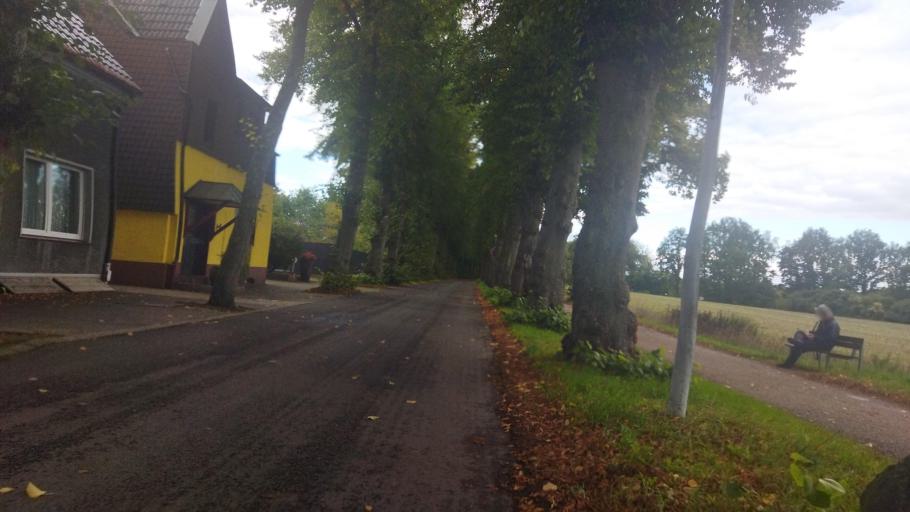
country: DE
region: North Rhine-Westphalia
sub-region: Regierungsbezirk Munster
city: Haltern
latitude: 51.7502
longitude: 7.2042
